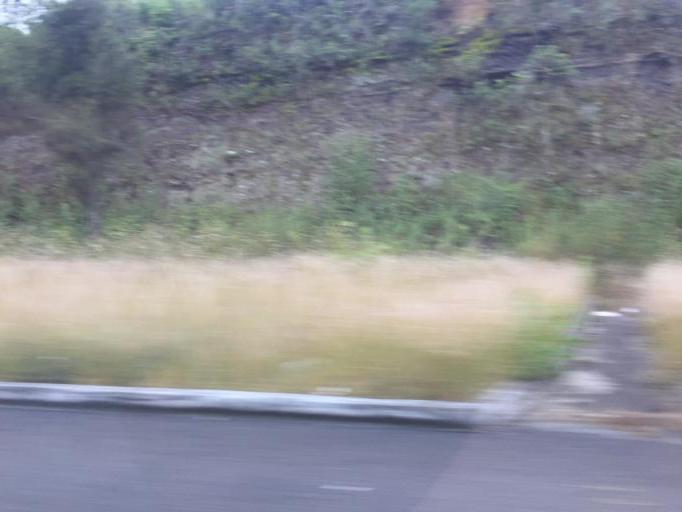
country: MX
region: Michoacan
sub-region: Puruandiro
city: San Lorenzo
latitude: 19.9606
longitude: -101.6785
